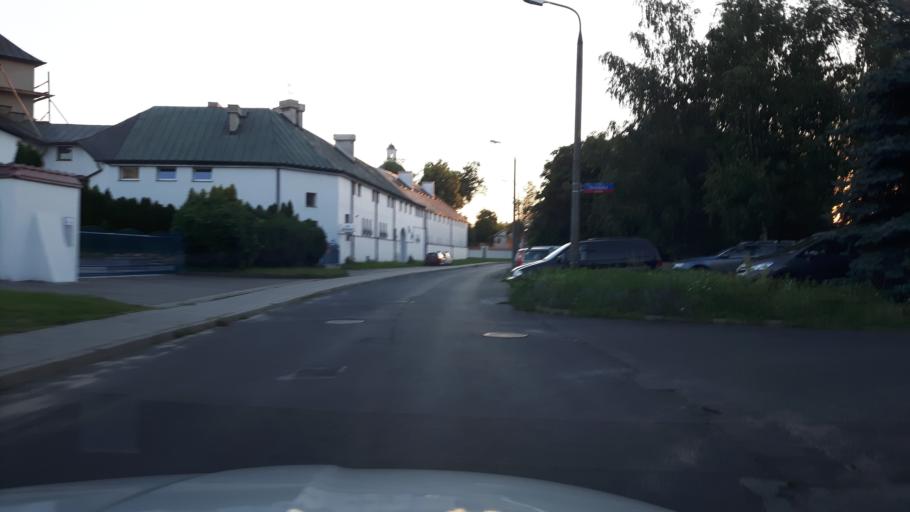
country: PL
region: Masovian Voivodeship
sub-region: Warszawa
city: Mokotow
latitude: 52.1941
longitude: 21.0581
